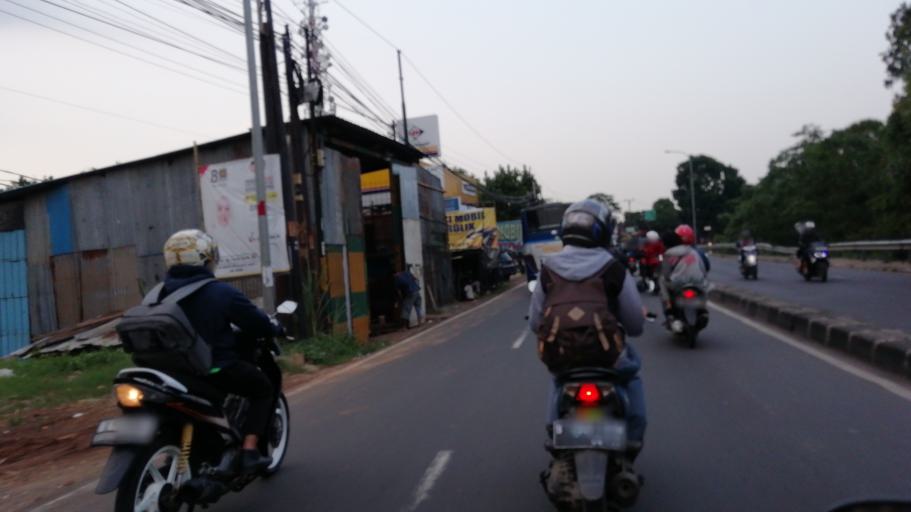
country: ID
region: West Java
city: Cibinong
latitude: -6.4380
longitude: 106.8521
